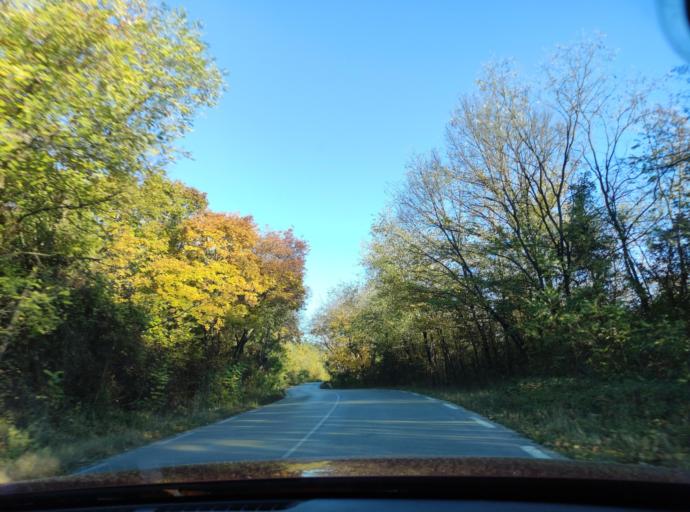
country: BG
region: Montana
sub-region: Obshtina Montana
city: Montana
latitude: 43.4042
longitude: 23.0771
